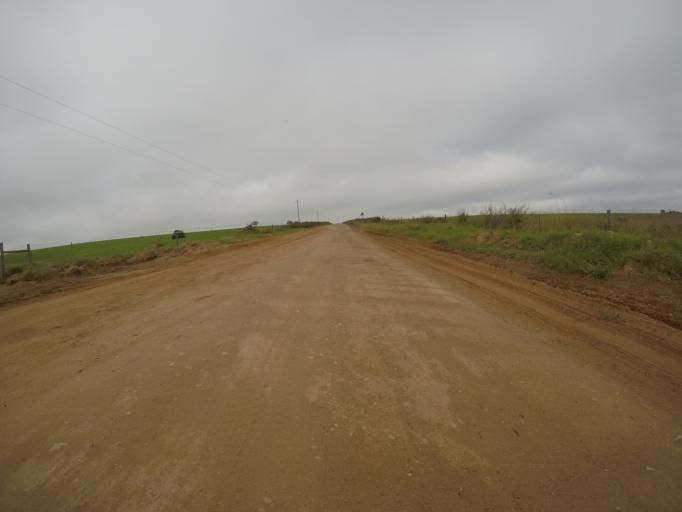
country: ZA
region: Eastern Cape
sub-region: Cacadu District Municipality
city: Kareedouw
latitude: -34.0193
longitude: 24.2394
